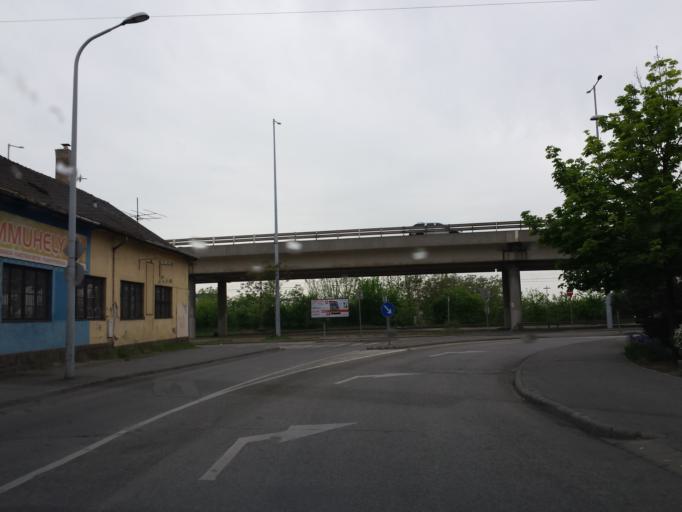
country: HU
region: Budapest
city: Budapest XX. keruelet
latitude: 47.4313
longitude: 19.1014
